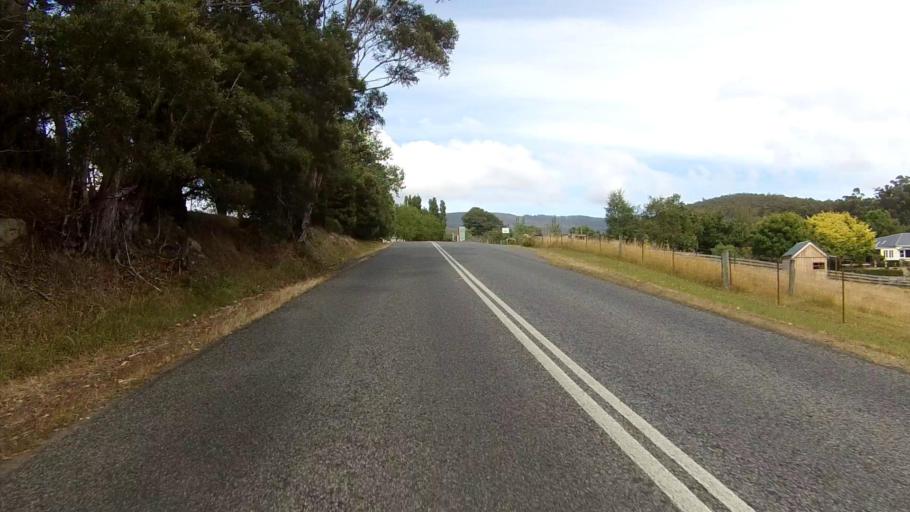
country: AU
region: Tasmania
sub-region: Kingborough
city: Kettering
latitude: -43.1341
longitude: 147.2509
